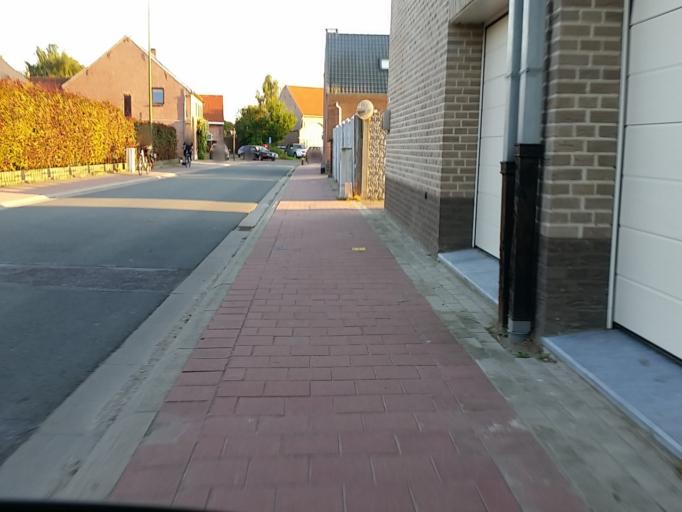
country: BE
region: Flanders
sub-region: Provincie Vlaams-Brabant
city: Kampenhout
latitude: 50.9593
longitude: 4.5562
